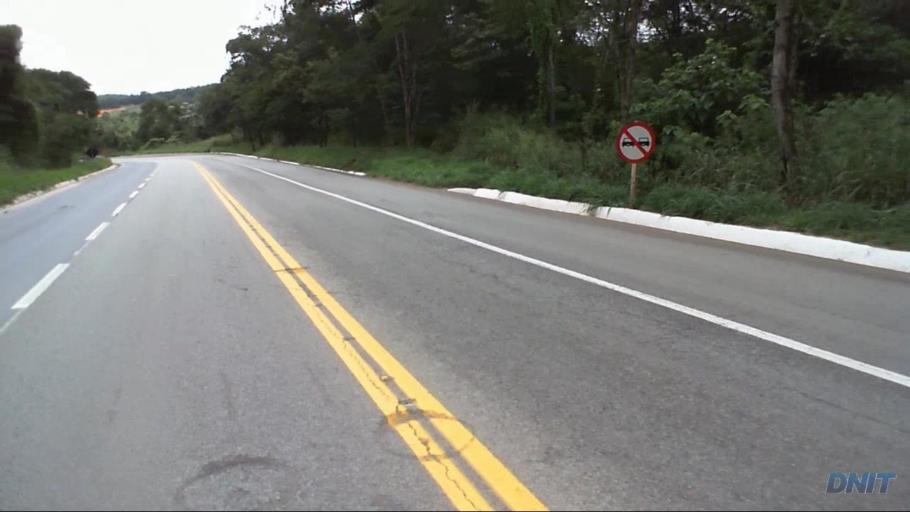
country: BR
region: Minas Gerais
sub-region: Barao De Cocais
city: Barao de Cocais
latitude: -19.7361
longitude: -43.5135
